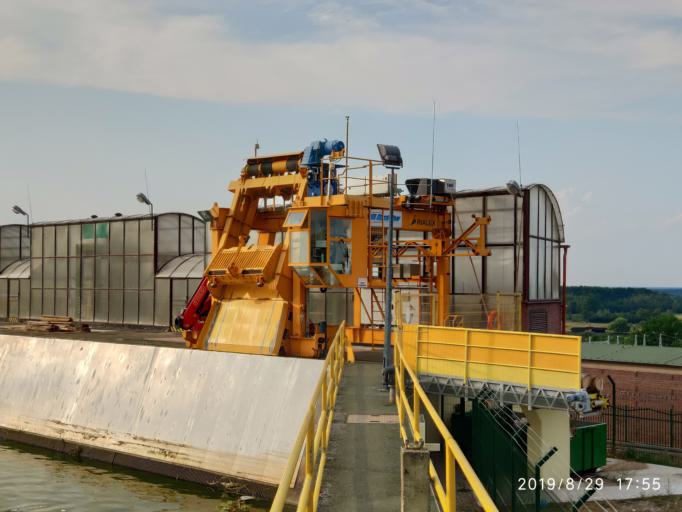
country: PL
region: Lubusz
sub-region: Powiat krosnienski
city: Bobrowice
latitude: 51.9875
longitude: 15.0543
